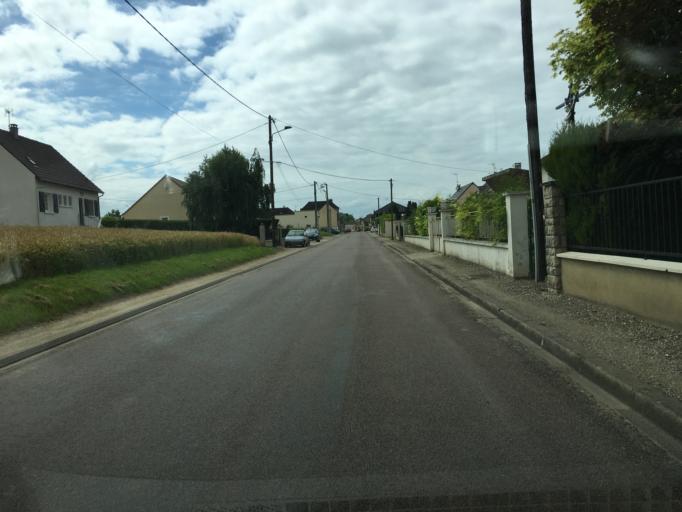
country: FR
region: Bourgogne
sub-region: Departement de l'Yonne
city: Laroche-Saint-Cydroine
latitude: 47.9506
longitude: 3.4417
